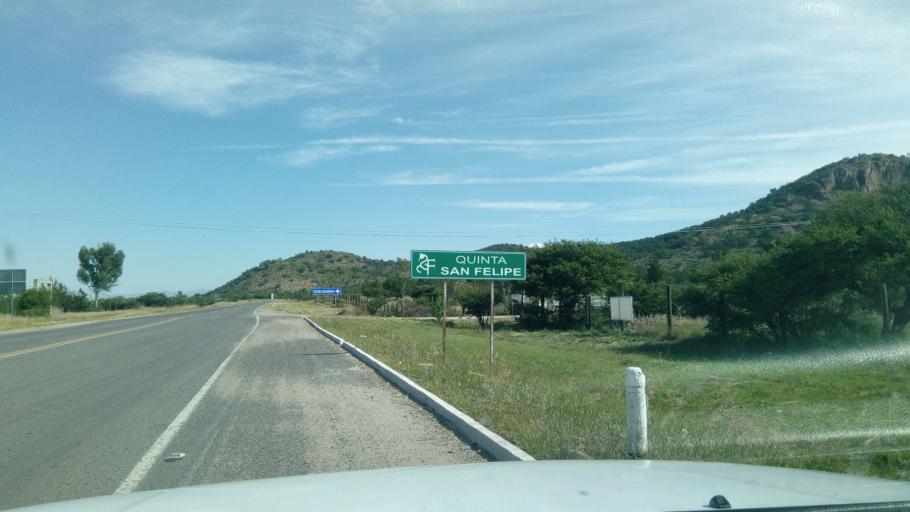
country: MX
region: Durango
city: Victoria de Durango
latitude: 24.1571
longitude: -104.7054
